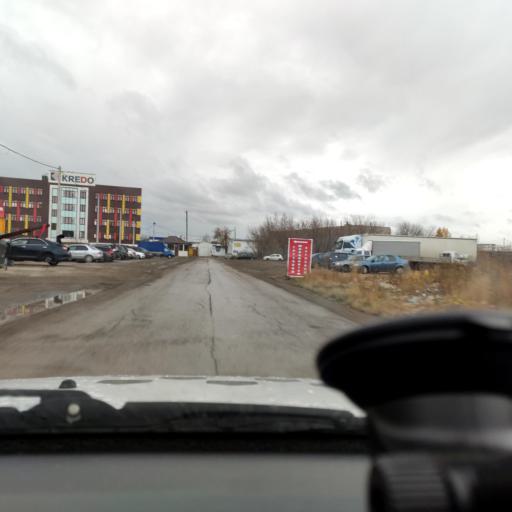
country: RU
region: Perm
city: Kondratovo
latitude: 57.9455
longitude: 56.1461
